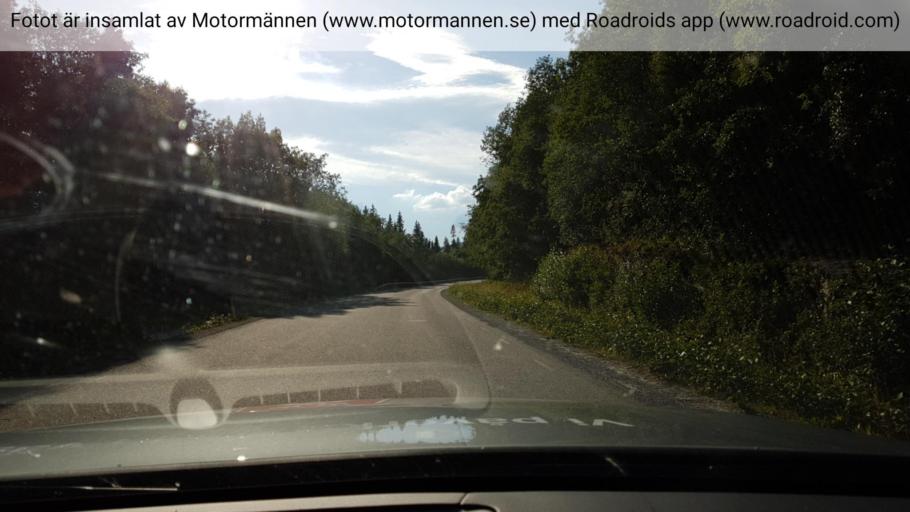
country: SE
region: Jaemtland
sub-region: Are Kommun
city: Are
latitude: 63.4105
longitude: 13.0451
